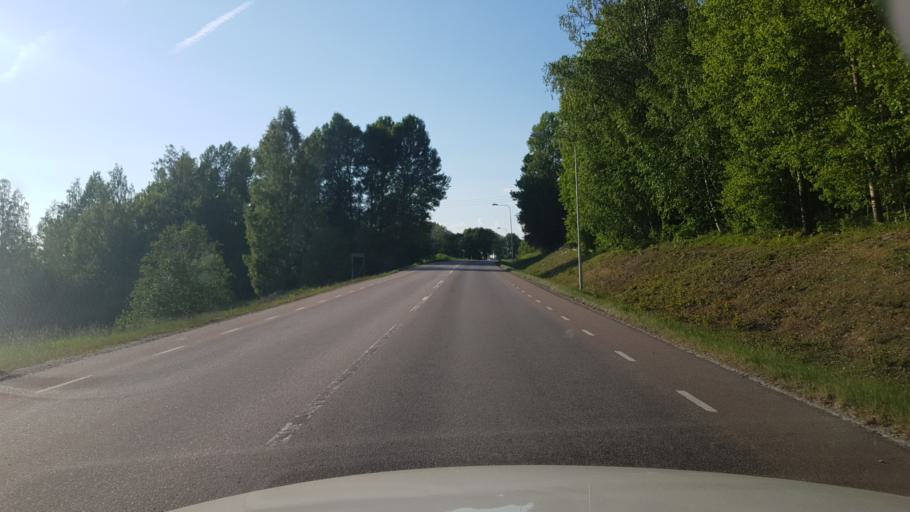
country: SE
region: Vaestmanland
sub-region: Kopings Kommun
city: Kolsva
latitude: 59.6074
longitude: 15.8306
